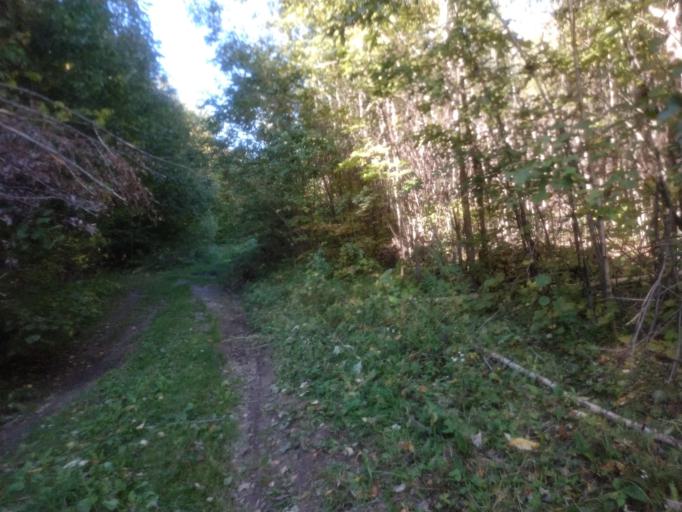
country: RU
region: Chuvashia
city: Novyye Lapsary
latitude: 56.1407
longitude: 47.1374
